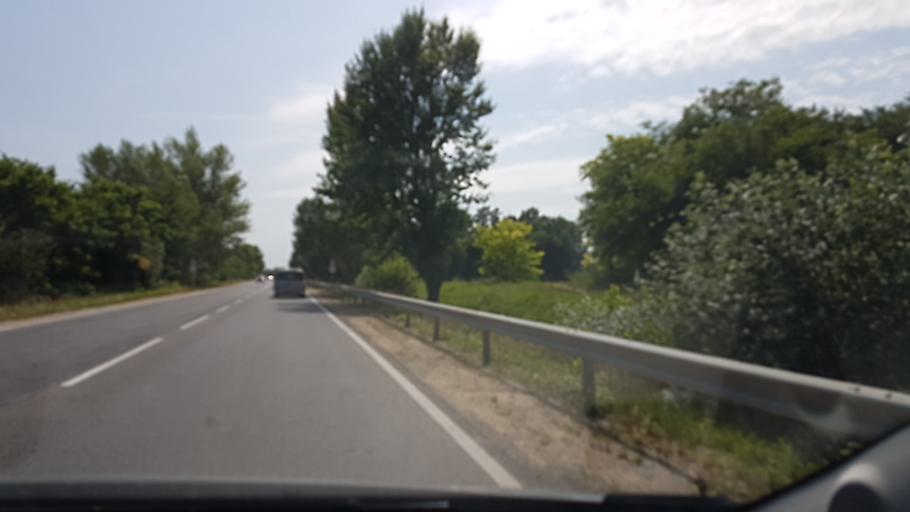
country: HU
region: Pest
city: Dunaharaszti
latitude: 47.3327
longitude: 19.1052
